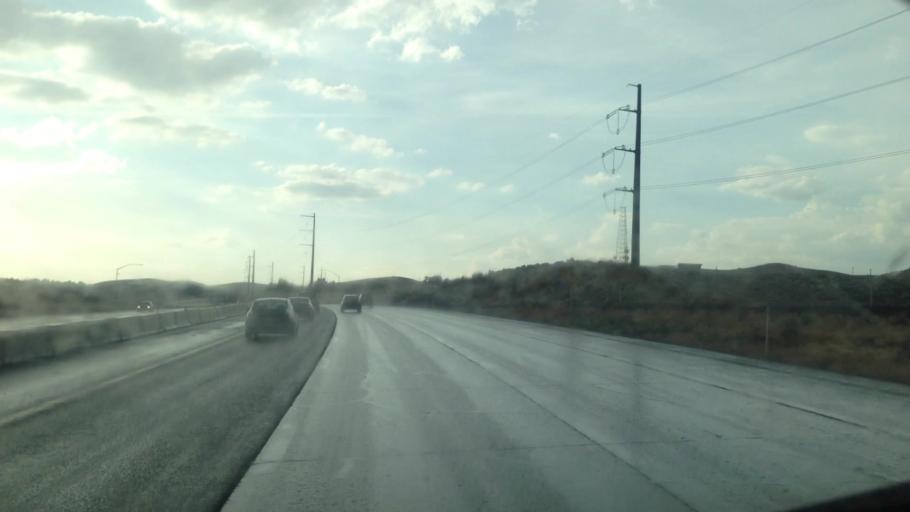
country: US
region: Nevada
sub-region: Washoe County
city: Sun Valley
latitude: 39.5751
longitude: -119.8095
